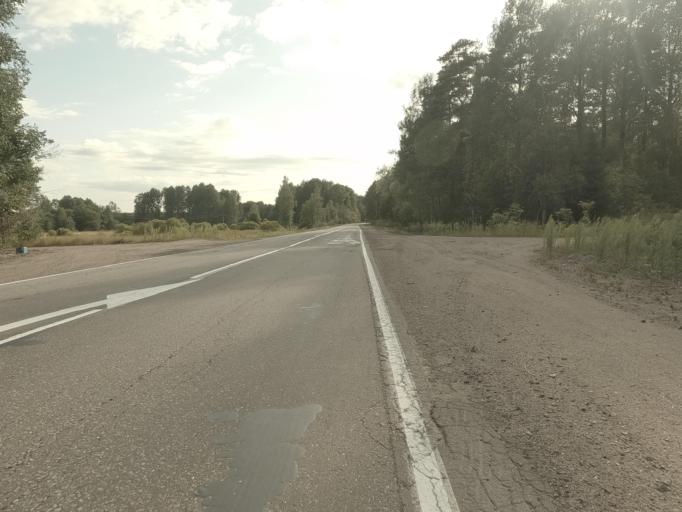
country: RU
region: Leningrad
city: Kamennogorsk
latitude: 60.8737
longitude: 28.9972
